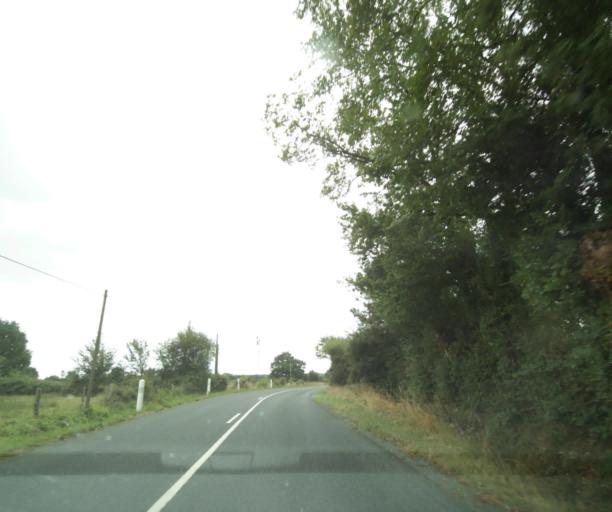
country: FR
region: Pays de la Loire
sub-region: Departement de la Sarthe
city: Precigne
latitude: 47.7543
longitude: -0.3055
